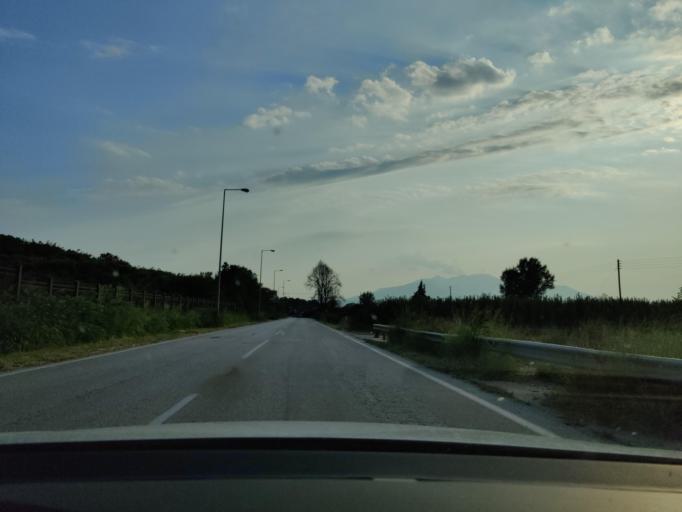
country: GR
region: East Macedonia and Thrace
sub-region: Nomos Kavalas
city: Amygdaleonas
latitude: 40.9737
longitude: 24.3577
